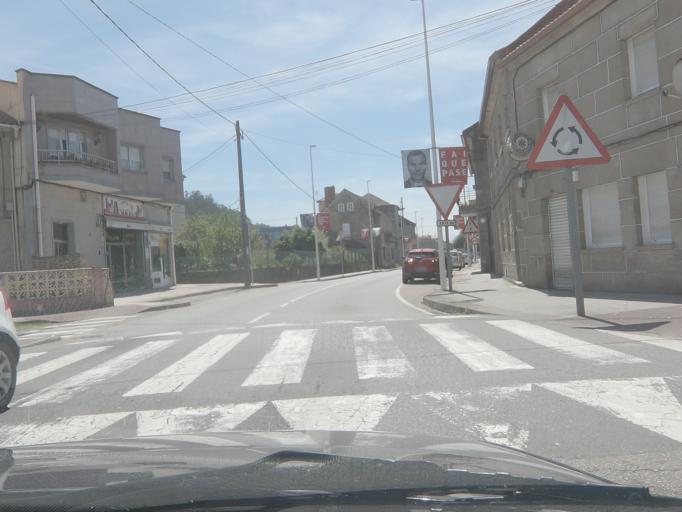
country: ES
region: Galicia
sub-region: Provincia de Pontevedra
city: Pontevedra
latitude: 42.4179
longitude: -8.6337
